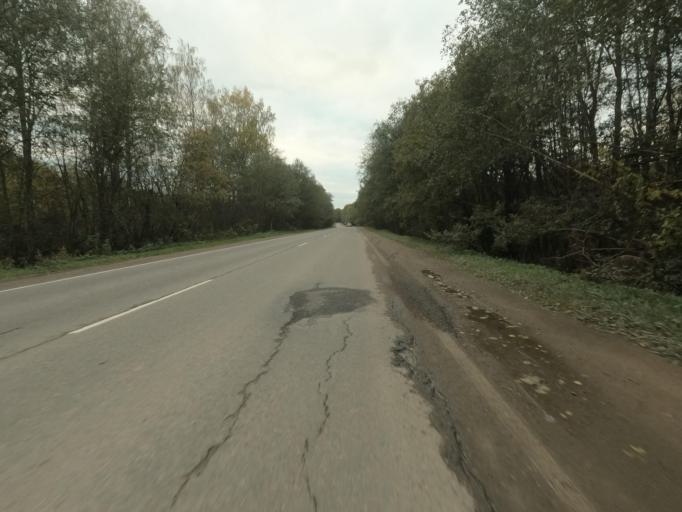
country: RU
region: Leningrad
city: Pavlovo
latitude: 59.7941
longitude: 30.9541
